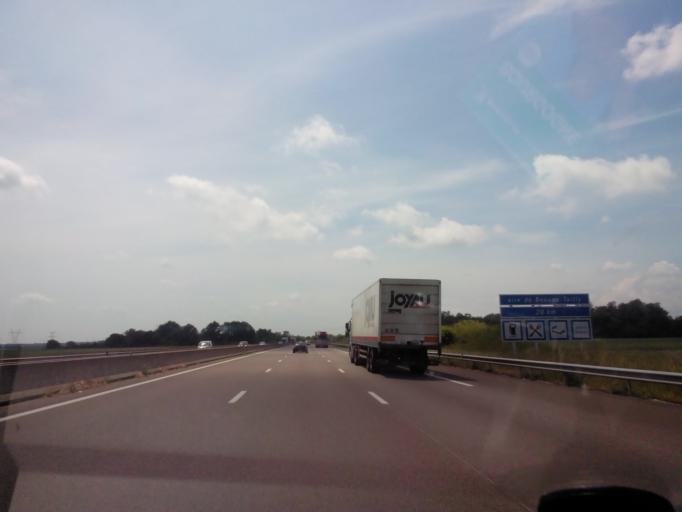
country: FR
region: Bourgogne
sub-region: Departement de la Cote-d'Or
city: Nuits-Saint-Georges
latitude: 47.1148
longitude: 4.9617
